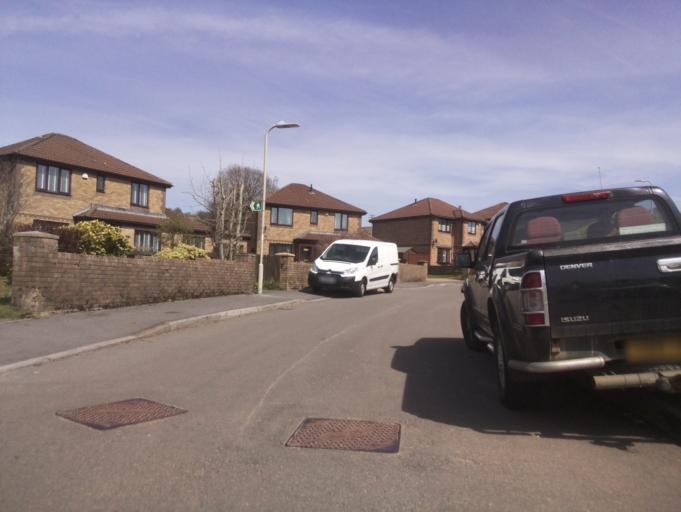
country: GB
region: Wales
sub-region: Merthyr Tydfil County Borough
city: Merthyr Tydfil
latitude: 51.7753
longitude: -3.3579
